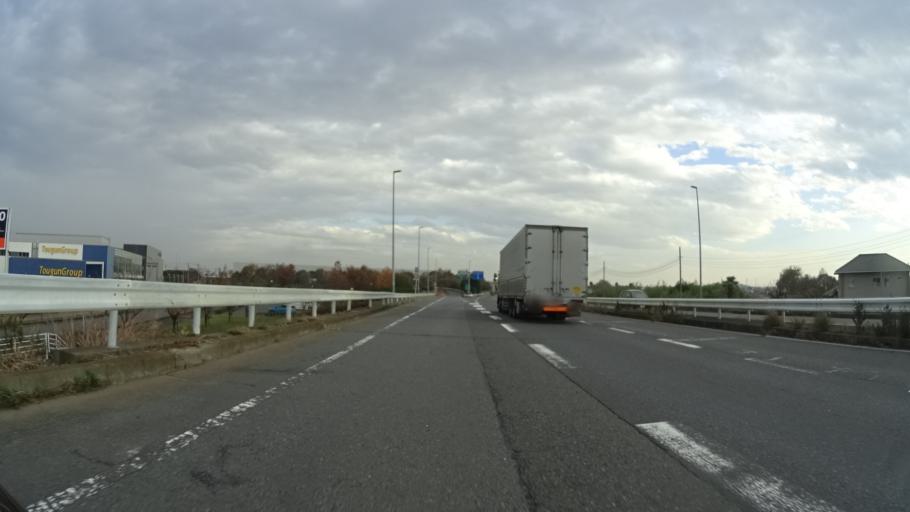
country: JP
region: Gunma
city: Isesaki
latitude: 36.3528
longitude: 139.2164
